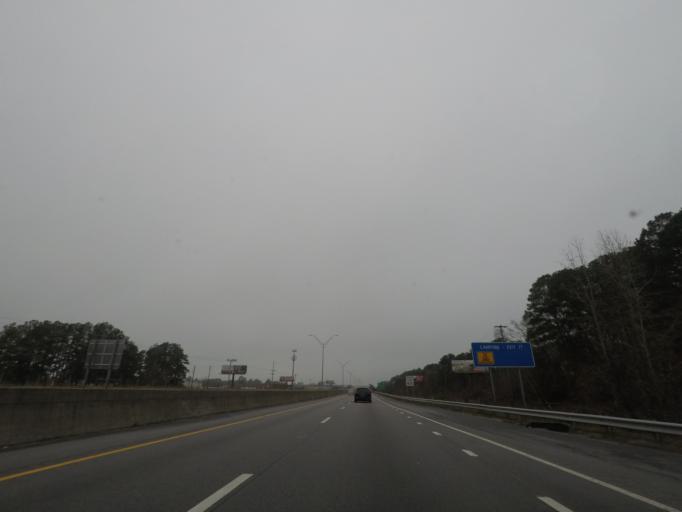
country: US
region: North Carolina
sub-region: Robeson County
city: Lumberton
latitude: 34.6314
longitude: -79.0319
